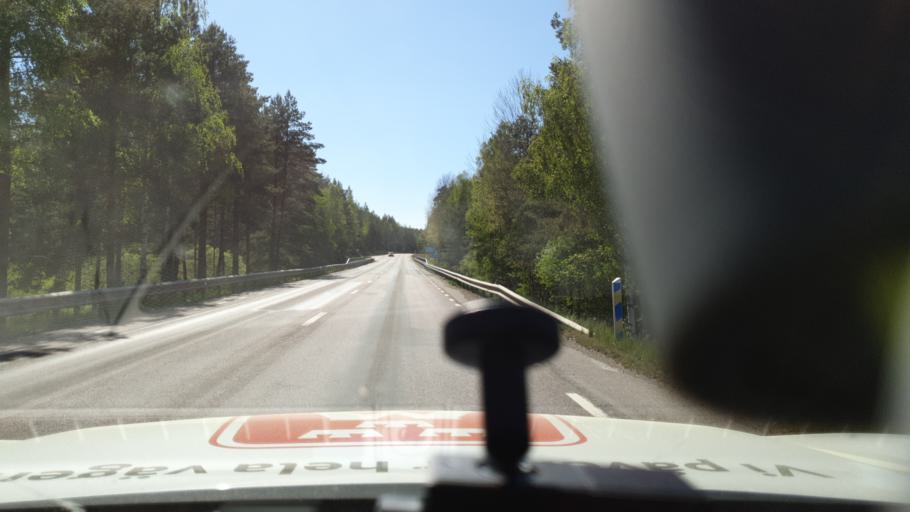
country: SE
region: Kalmar
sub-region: Hultsfreds Kommun
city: Virserum
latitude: 57.4066
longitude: 15.5312
